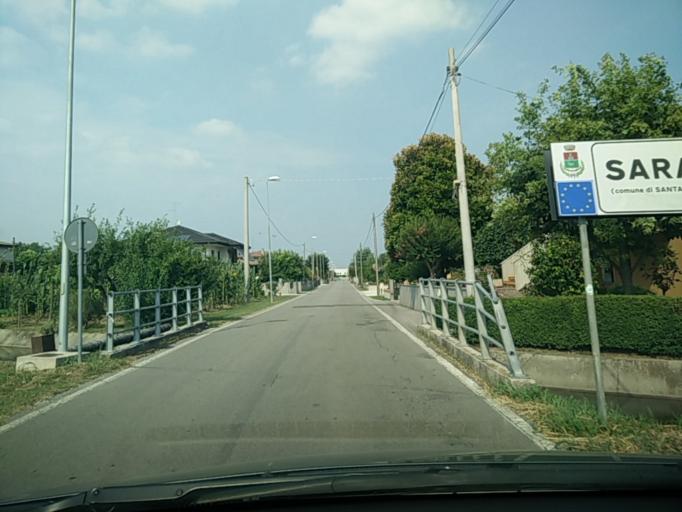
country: IT
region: Veneto
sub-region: Provincia di Treviso
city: Santa Lucia di Piave
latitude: 45.8633
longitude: 12.2902
